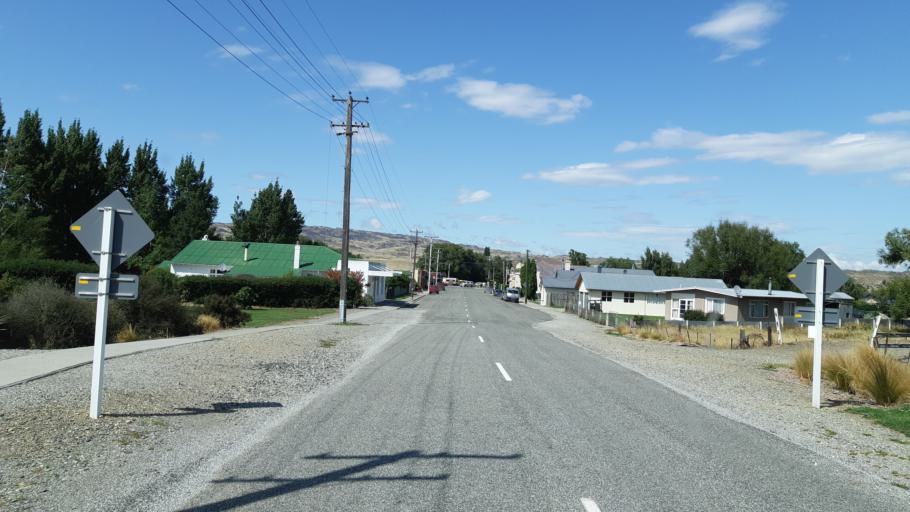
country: NZ
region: Otago
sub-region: Queenstown-Lakes District
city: Wanaka
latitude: -45.0921
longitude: 169.6019
